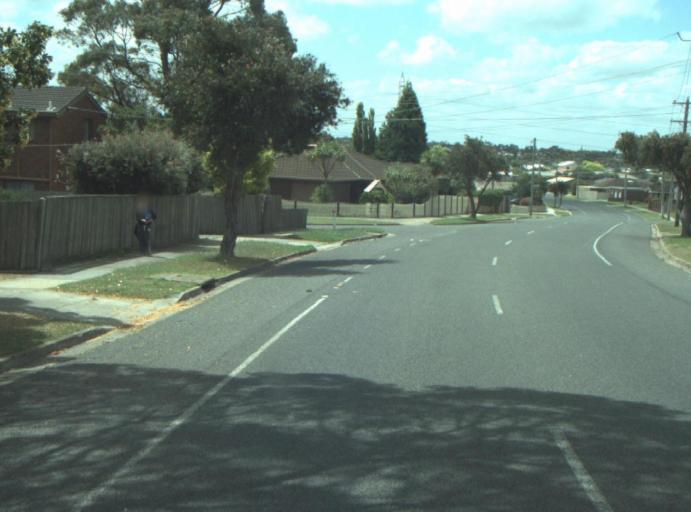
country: AU
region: Victoria
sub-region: Greater Geelong
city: Wandana Heights
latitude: -38.2005
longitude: 144.3314
